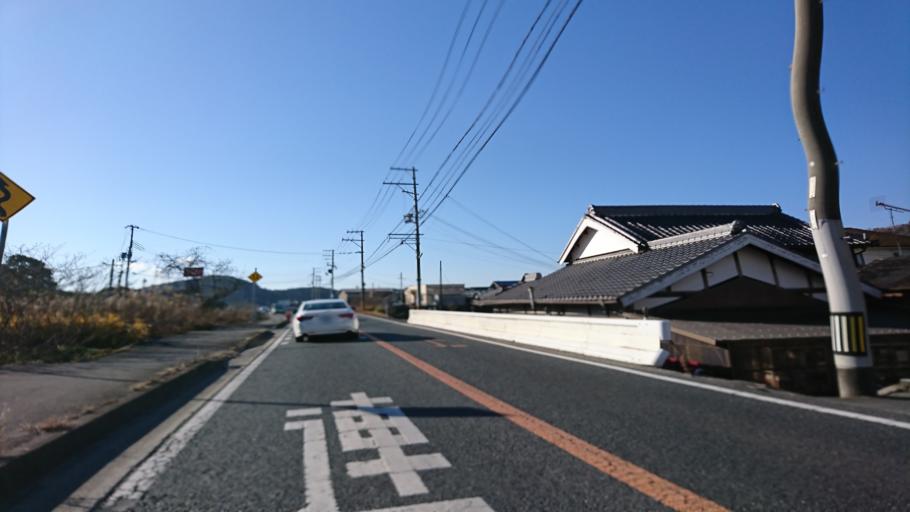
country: JP
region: Hyogo
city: Kakogawacho-honmachi
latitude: 34.8097
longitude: 134.8360
